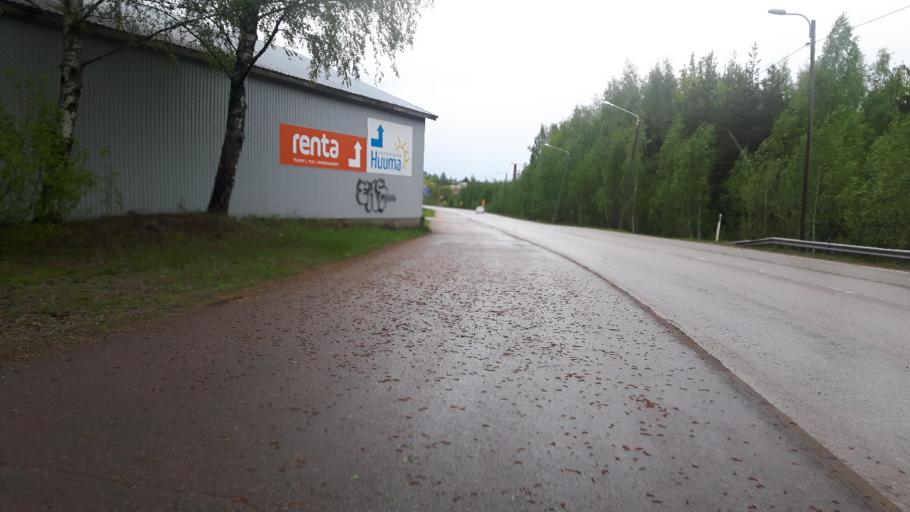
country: FI
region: Kymenlaakso
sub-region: Kotka-Hamina
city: Kotka
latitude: 60.4985
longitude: 26.9034
